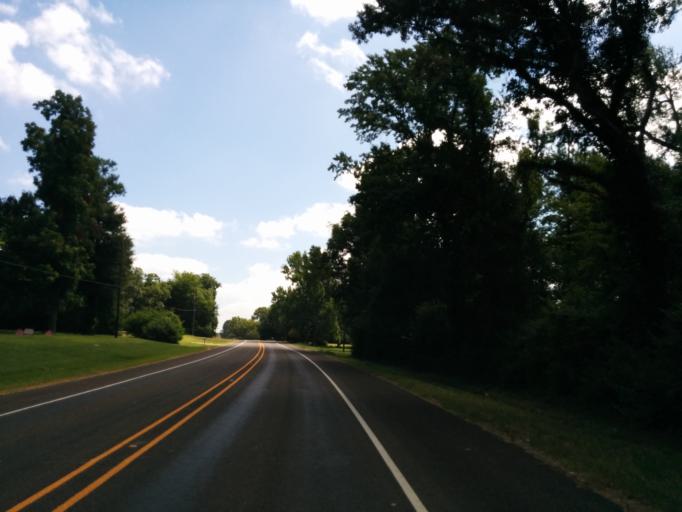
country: US
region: Texas
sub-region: Houston County
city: Crockett
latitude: 31.3306
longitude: -95.4346
